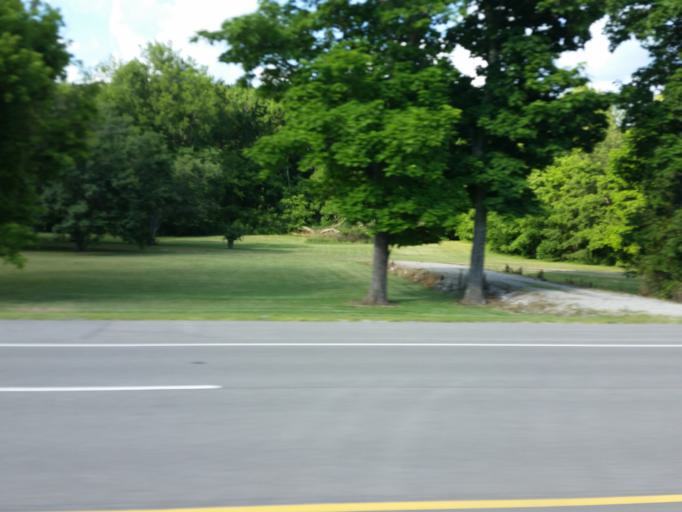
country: US
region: Tennessee
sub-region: Lewis County
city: Hohenwald
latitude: 35.5698
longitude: -87.4241
